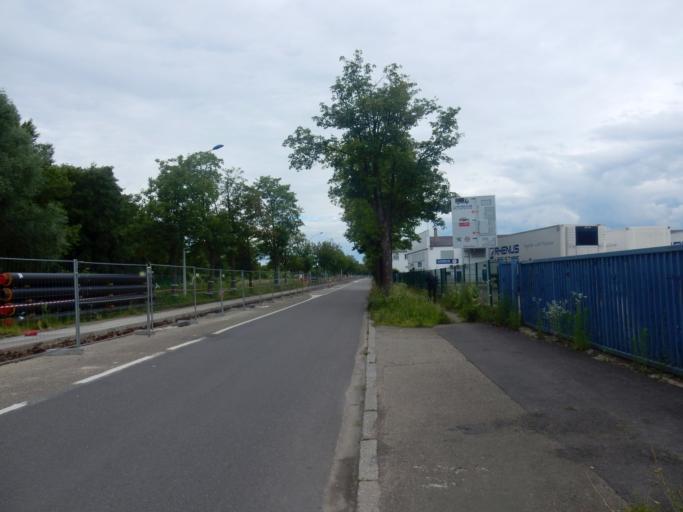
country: DE
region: Baden-Wuerttemberg
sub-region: Freiburg Region
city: Kehl
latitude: 48.5608
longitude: 7.7890
